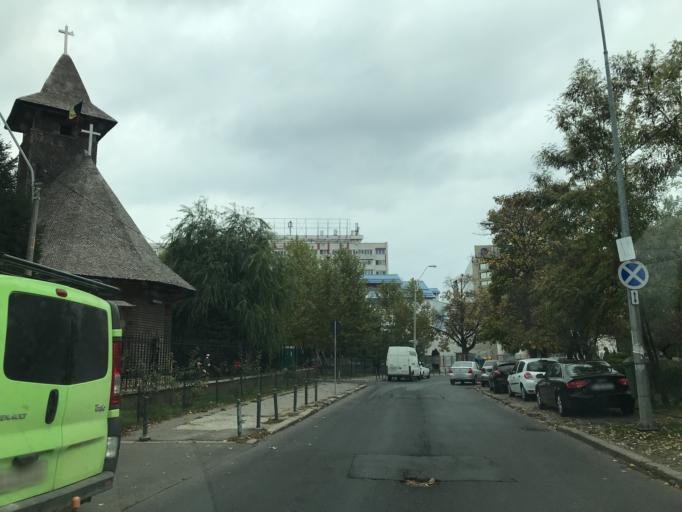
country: RO
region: Ilfov
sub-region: Comuna Chiajna
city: Rosu
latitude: 44.4825
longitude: 26.0598
